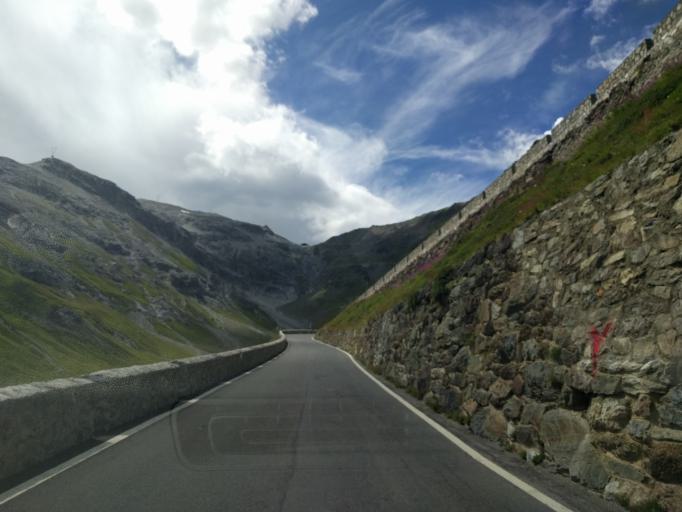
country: IT
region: Trentino-Alto Adige
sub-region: Bolzano
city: Stelvio
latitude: 46.5337
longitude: 10.4778
